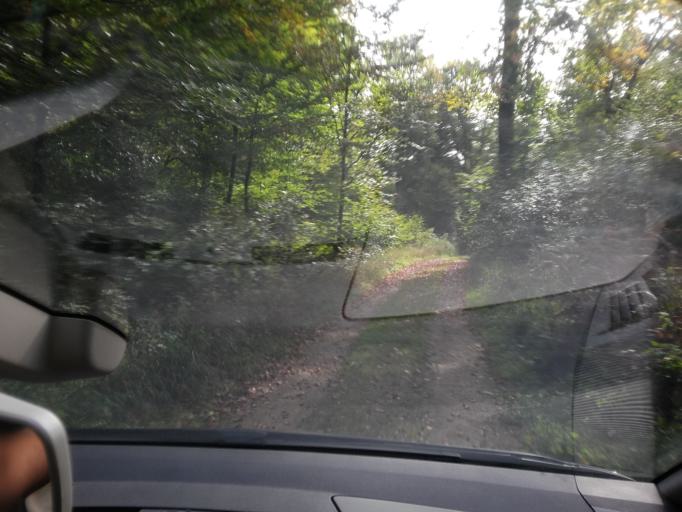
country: BE
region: Wallonia
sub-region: Province du Luxembourg
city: Attert
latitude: 49.7188
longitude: 5.7834
